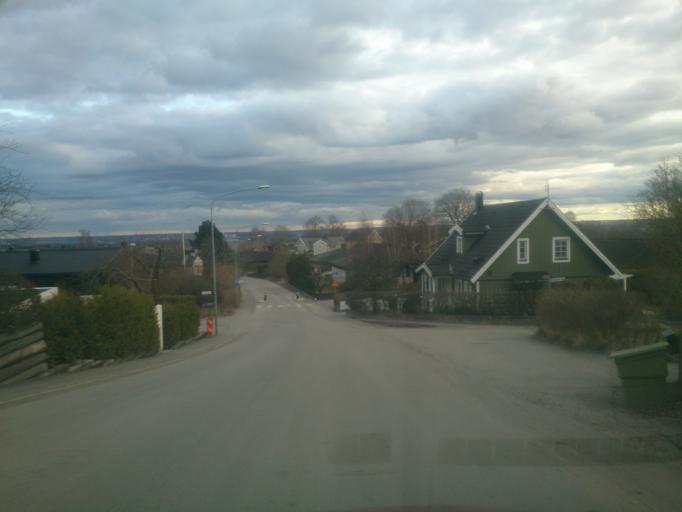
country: SE
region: OEstergoetland
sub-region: Norrkopings Kommun
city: Jursla
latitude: 58.6723
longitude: 16.1854
